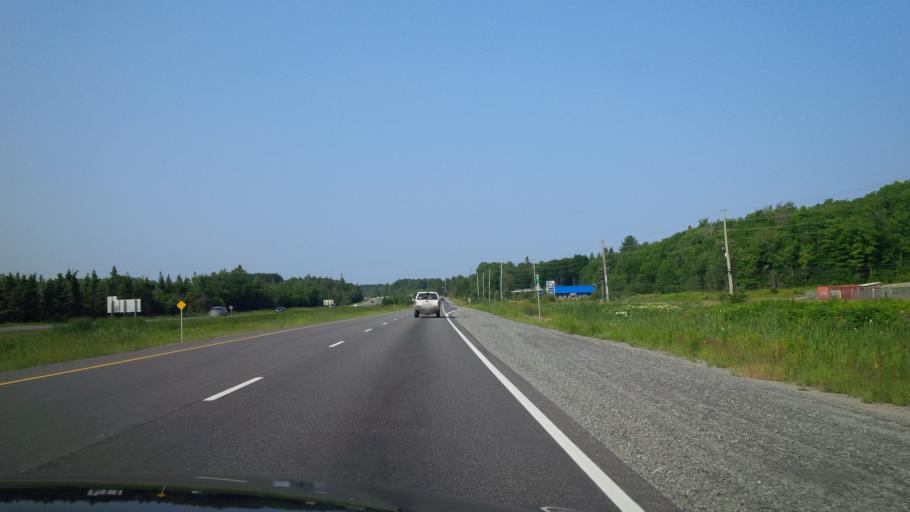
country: CA
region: Ontario
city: Huntsville
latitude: 45.3018
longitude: -79.2525
